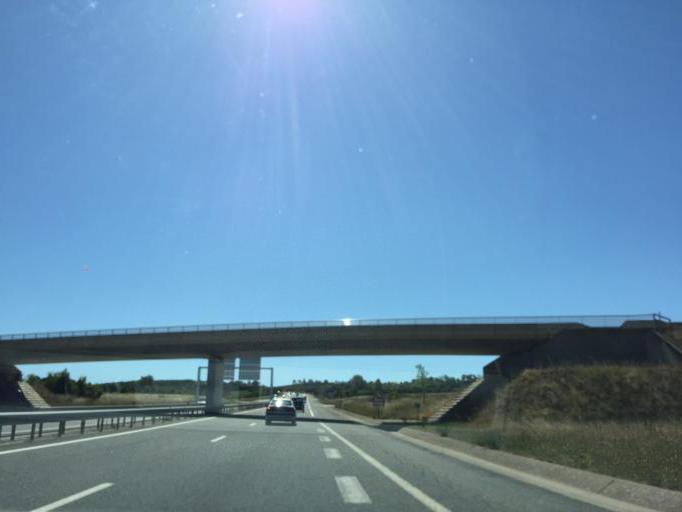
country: FR
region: Midi-Pyrenees
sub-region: Departement de l'Aveyron
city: La Cavalerie
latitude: 44.0080
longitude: 3.1453
